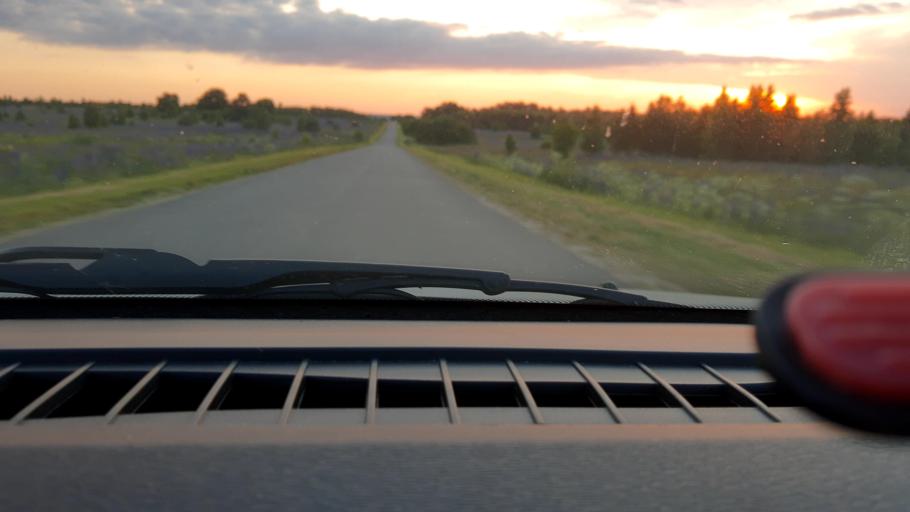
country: RU
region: Nizjnij Novgorod
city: Surovatikha
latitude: 55.8467
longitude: 43.9696
